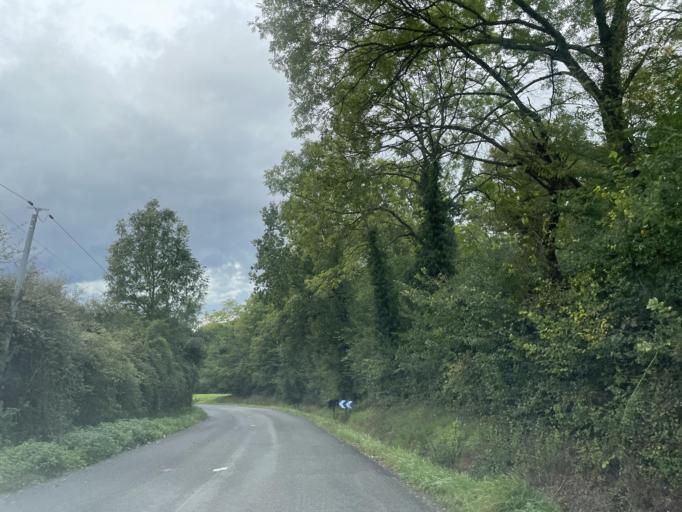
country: FR
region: Ile-de-France
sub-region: Departement de Seine-et-Marne
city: Trilport
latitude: 48.9391
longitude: 2.9645
